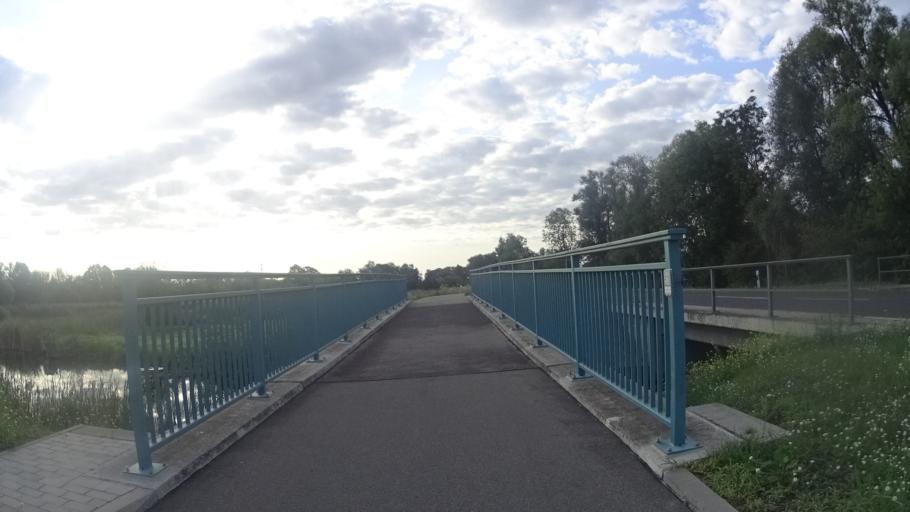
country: DE
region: Brandenburg
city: Premnitz
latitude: 52.5008
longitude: 12.4534
